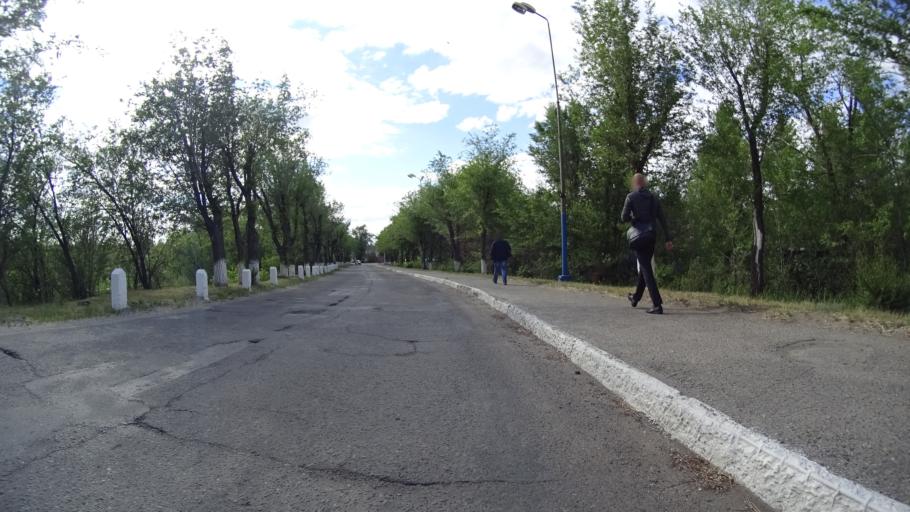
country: RU
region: Chelyabinsk
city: Troitsk
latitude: 54.0404
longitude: 61.6394
